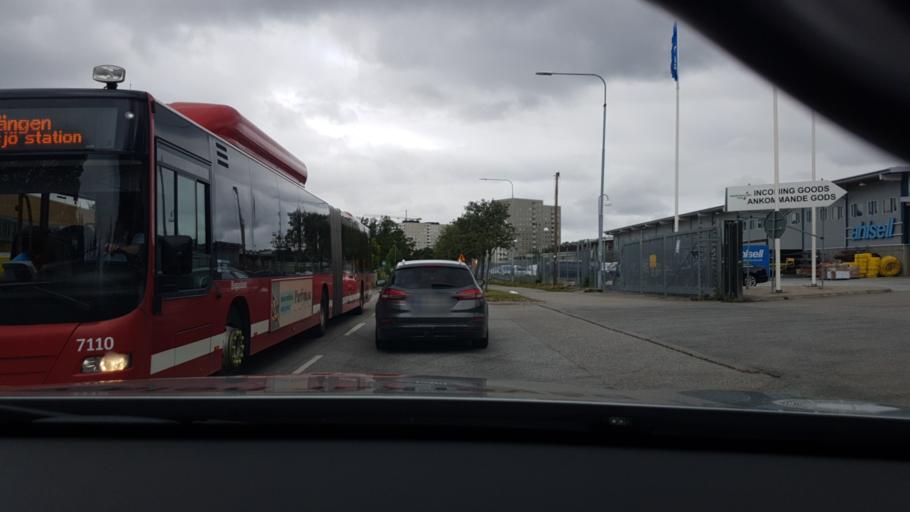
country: SE
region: Stockholm
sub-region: Stockholms Kommun
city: Arsta
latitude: 59.2894
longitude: 18.0599
